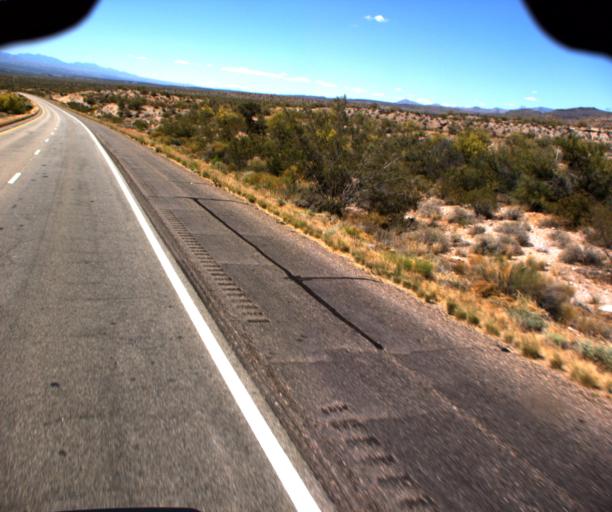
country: US
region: Arizona
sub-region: Yavapai County
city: Bagdad
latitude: 34.6187
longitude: -113.5294
